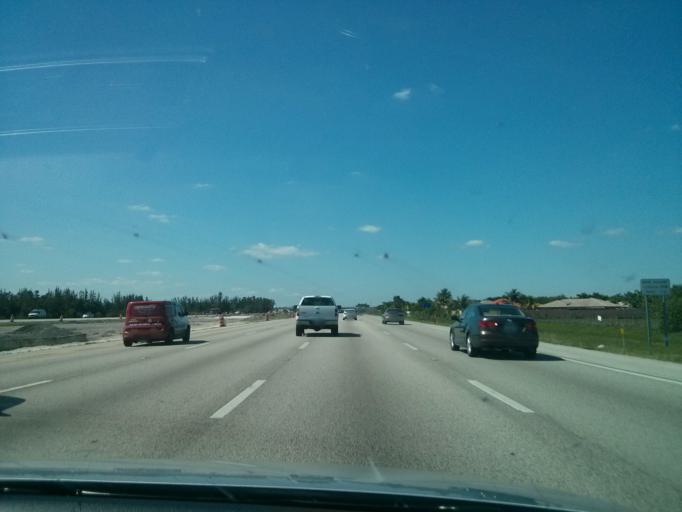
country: US
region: Florida
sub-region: Miami-Dade County
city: Palm Springs North
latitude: 25.9193
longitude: -80.3497
